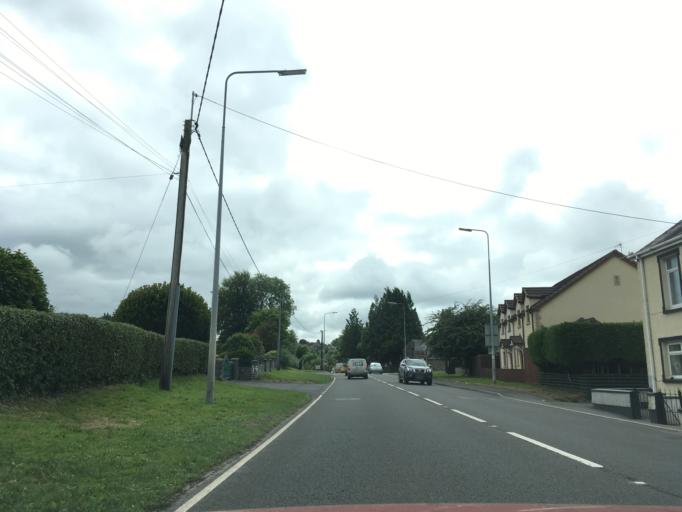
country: GB
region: Wales
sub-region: Carmarthenshire
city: Llandeilo
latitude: 51.8921
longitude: -3.9863
